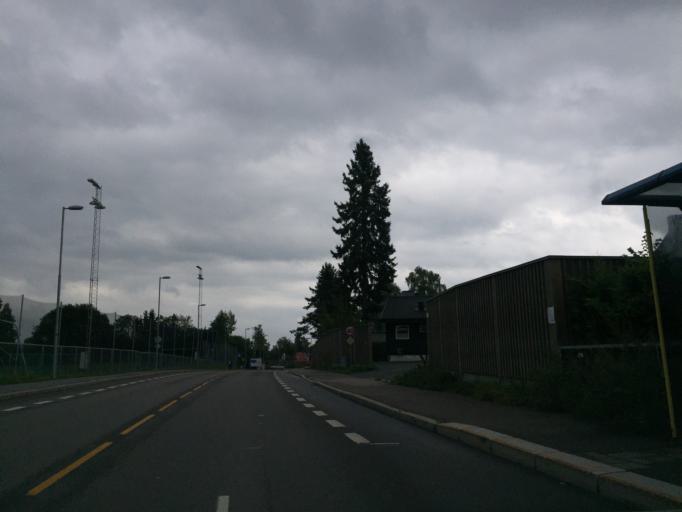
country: NO
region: Oslo
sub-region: Oslo
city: Sjolyststranda
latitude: 59.9507
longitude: 10.6752
